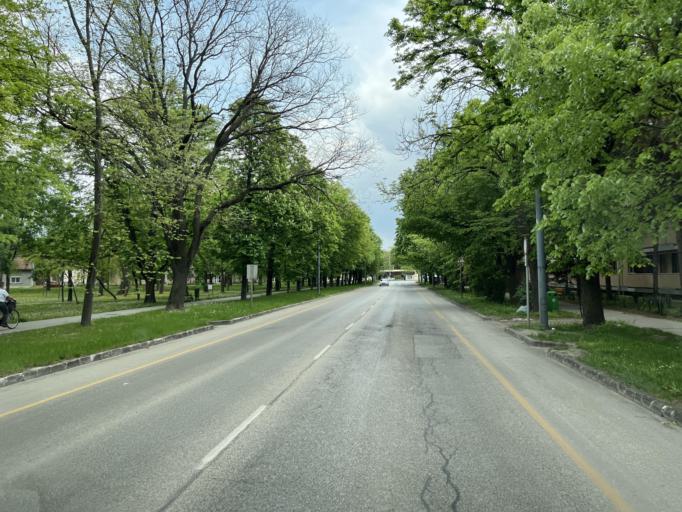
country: HU
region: Pest
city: Nagykoros
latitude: 47.0406
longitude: 19.7849
